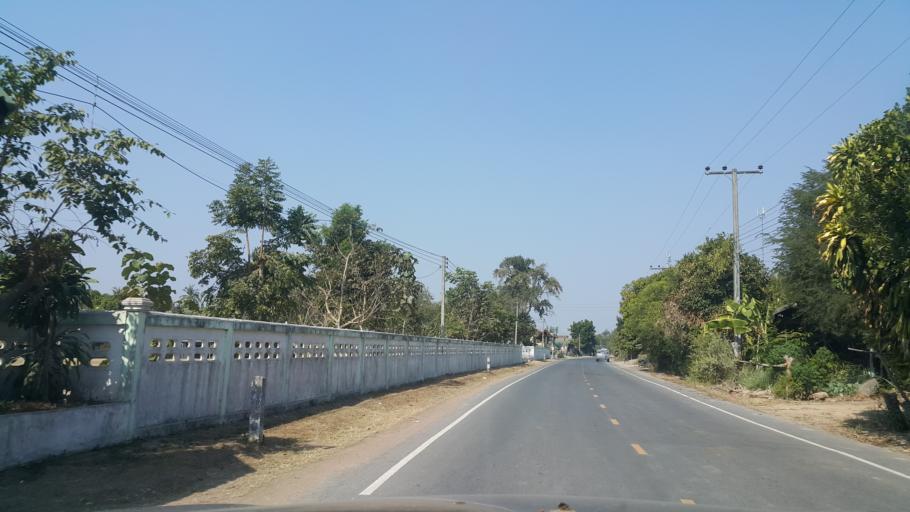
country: TH
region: Surin
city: Khwao Sinarin
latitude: 15.0425
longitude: 103.4267
